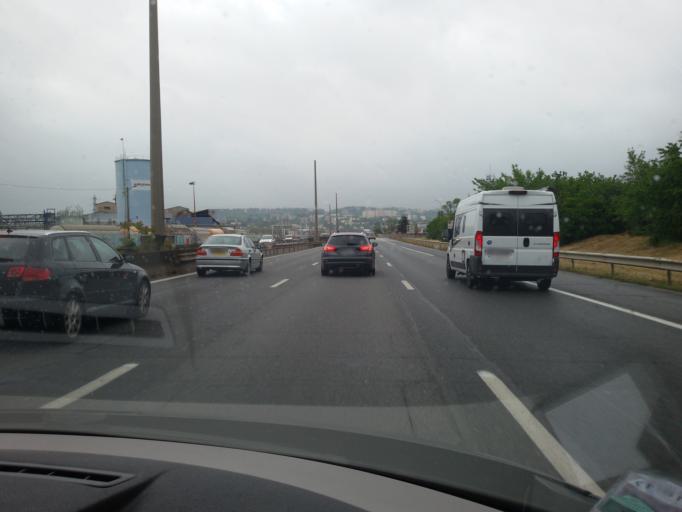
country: FR
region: Rhone-Alpes
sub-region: Departement du Rhone
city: Pierre-Benite
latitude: 45.7076
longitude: 4.8308
